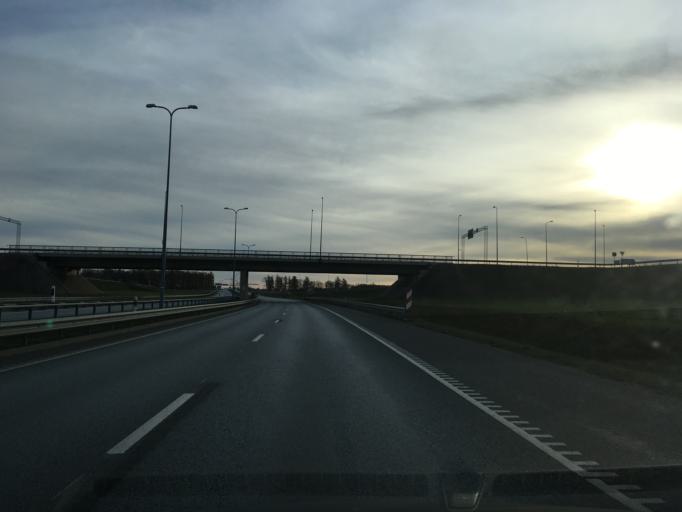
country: EE
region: Ida-Virumaa
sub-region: Kohtla-Jaerve linn
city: Kohtla-Jarve
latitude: 59.3869
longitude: 27.3459
